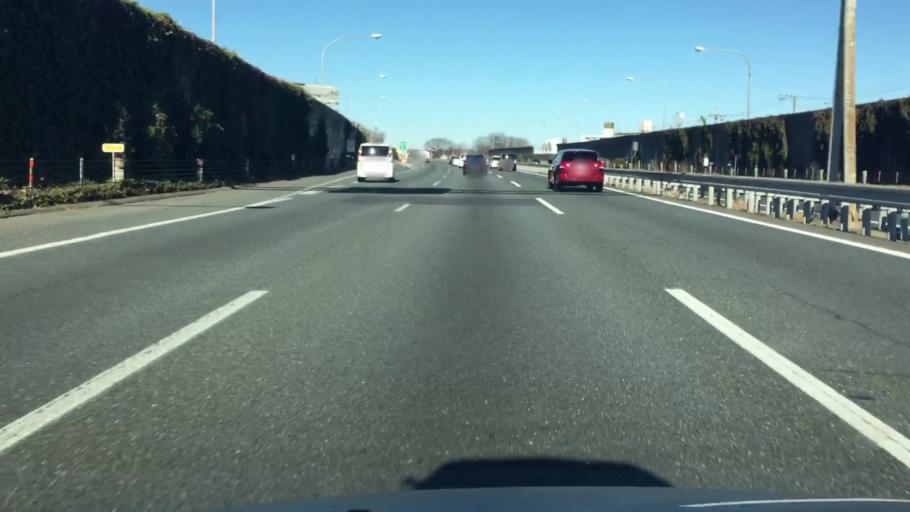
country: JP
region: Saitama
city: Sakado
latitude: 35.9430
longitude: 139.4014
